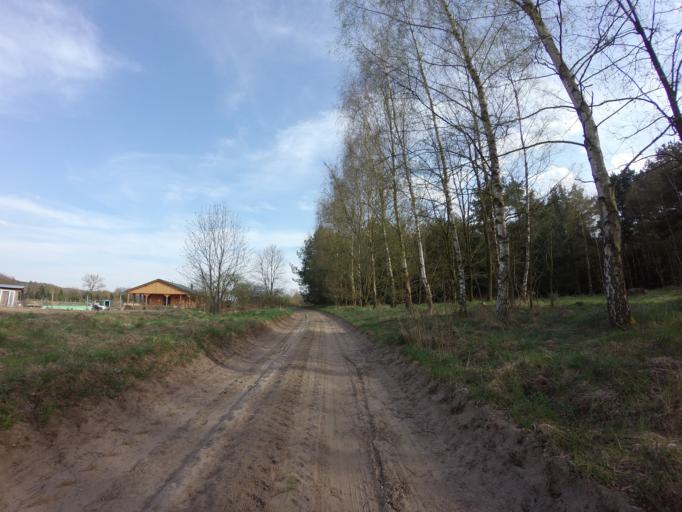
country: PL
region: West Pomeranian Voivodeship
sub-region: Powiat choszczenski
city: Recz
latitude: 53.1933
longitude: 15.4994
